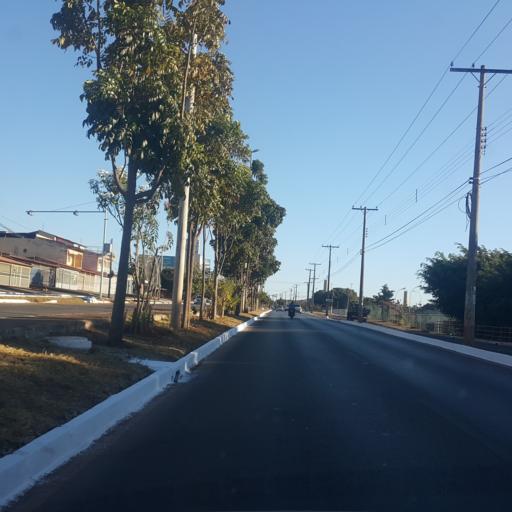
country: BR
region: Federal District
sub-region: Brasilia
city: Brasilia
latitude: -15.8192
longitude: -48.0956
